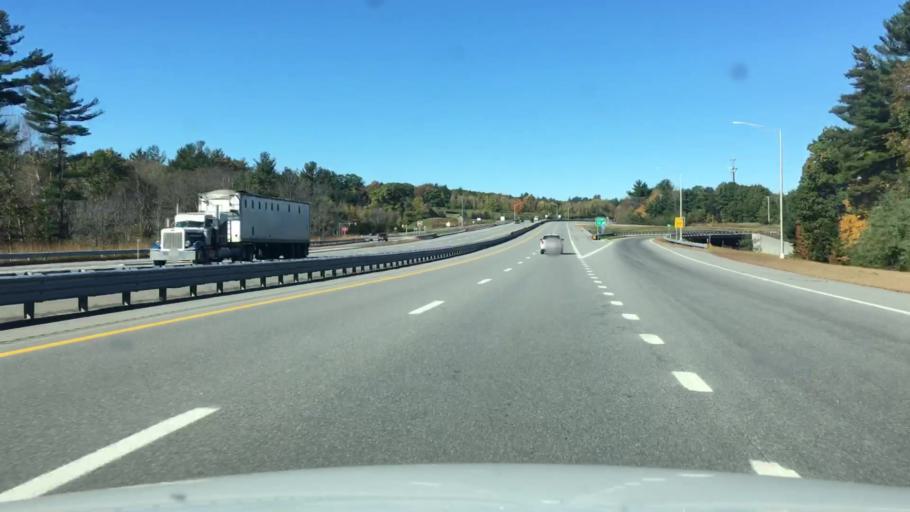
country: US
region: New Hampshire
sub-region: Strafford County
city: Rochester
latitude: 43.2810
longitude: -70.9753
